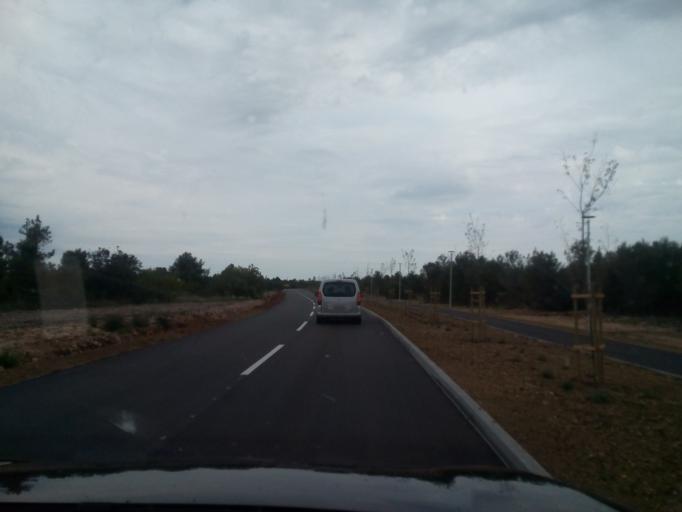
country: HR
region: Sibensko-Kniniska
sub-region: Grad Sibenik
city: Sibenik
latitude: 43.7868
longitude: 15.9671
